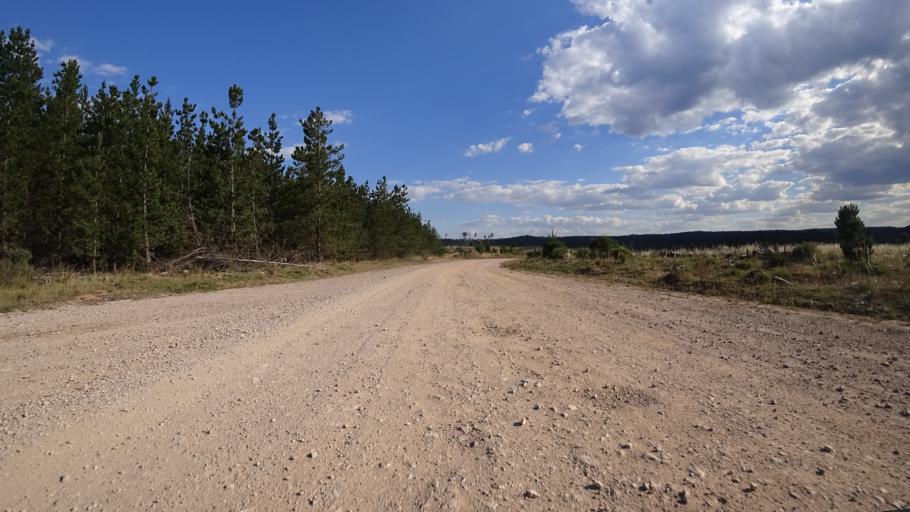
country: AU
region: New South Wales
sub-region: Lithgow
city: Lithgow
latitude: -33.3734
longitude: 150.2452
